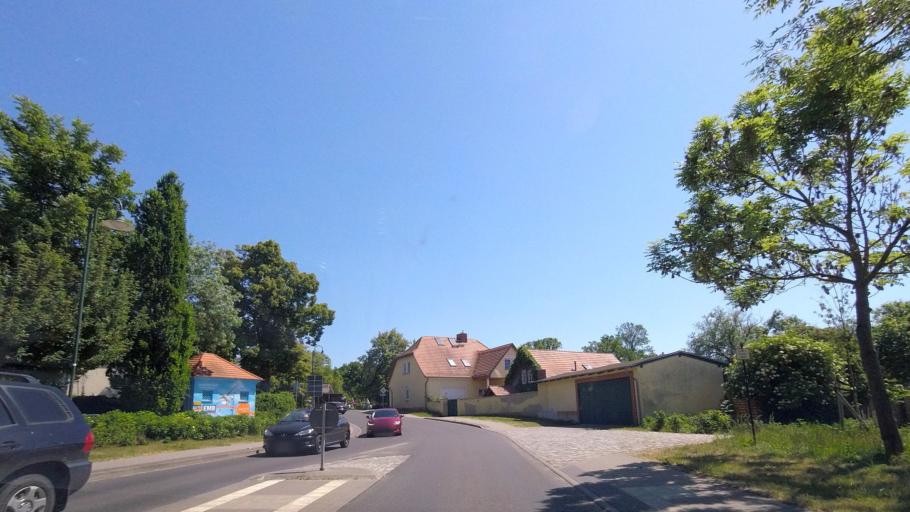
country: DE
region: Brandenburg
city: Werder
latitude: 52.3638
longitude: 12.9611
